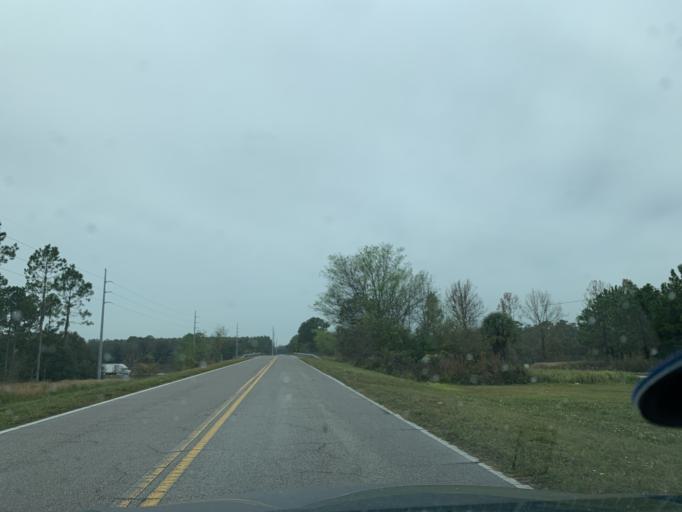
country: US
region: Florida
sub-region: Pasco County
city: Wesley Chapel
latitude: 28.2735
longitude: -82.3253
